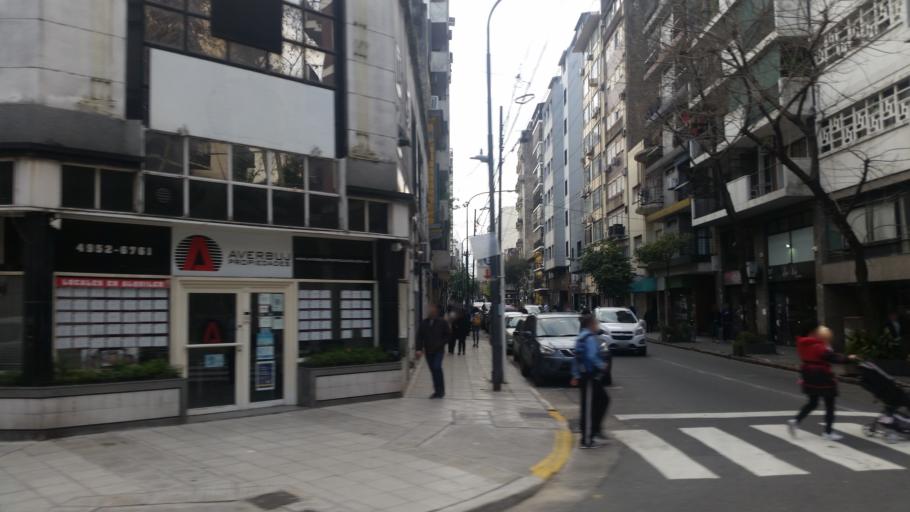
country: AR
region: Buenos Aires F.D.
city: Buenos Aires
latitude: -34.6059
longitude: -58.3965
